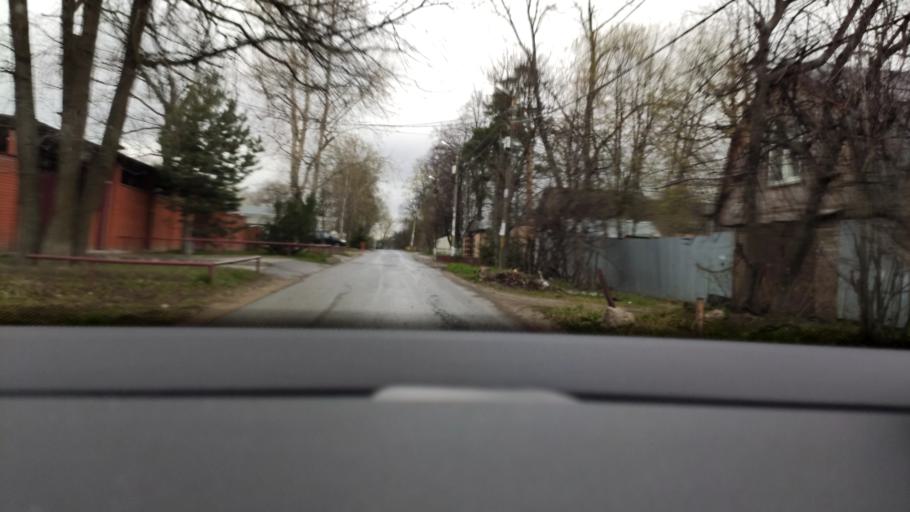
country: RU
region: Moskovskaya
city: Reutov
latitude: 55.7728
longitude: 37.8888
